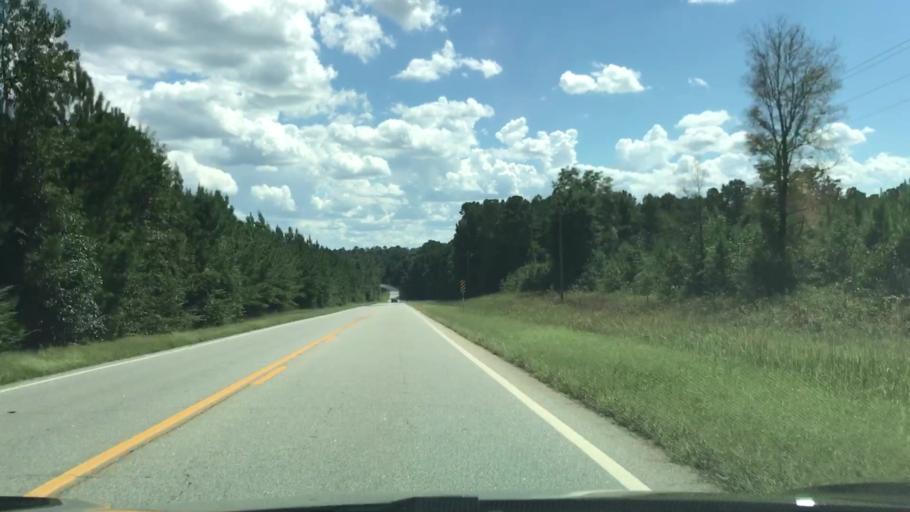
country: US
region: Georgia
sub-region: Greene County
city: Greensboro
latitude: 33.5954
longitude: -83.1960
